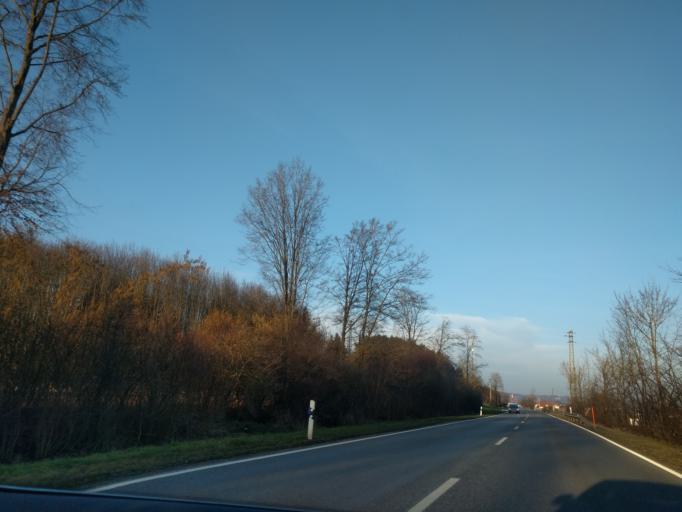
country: DE
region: Bavaria
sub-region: Swabia
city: Donauwoerth
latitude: 48.6960
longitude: 10.7376
